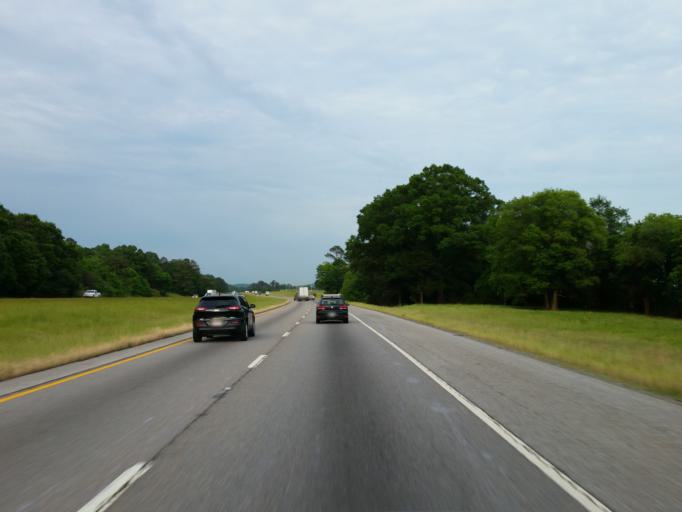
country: US
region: Alabama
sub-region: Talladega County
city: Lincoln
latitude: 33.5846
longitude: -86.0736
